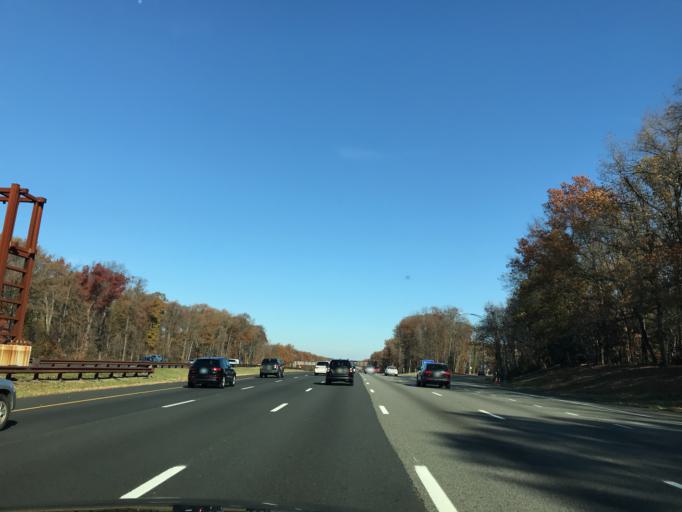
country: US
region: New Jersey
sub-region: Middlesex County
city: Iselin
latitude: 40.5891
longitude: -74.3257
